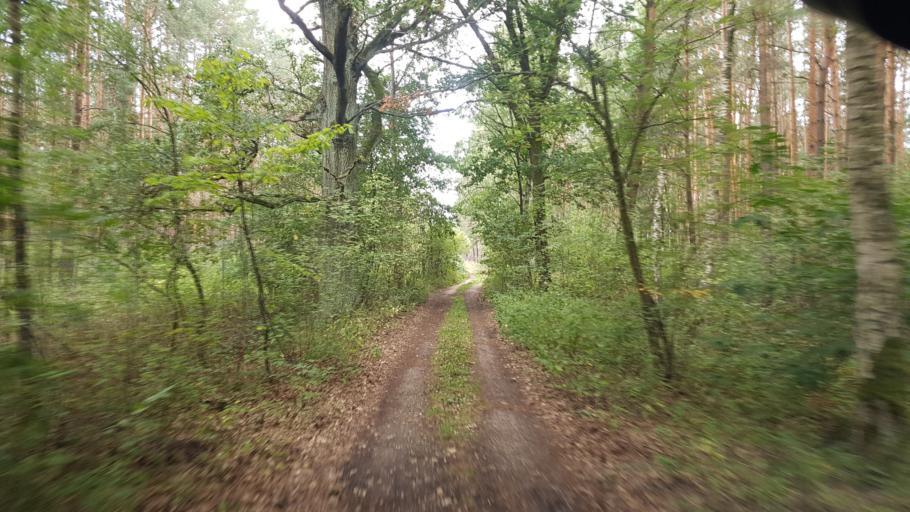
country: DE
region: Brandenburg
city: Ruckersdorf
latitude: 51.5787
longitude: 13.6001
